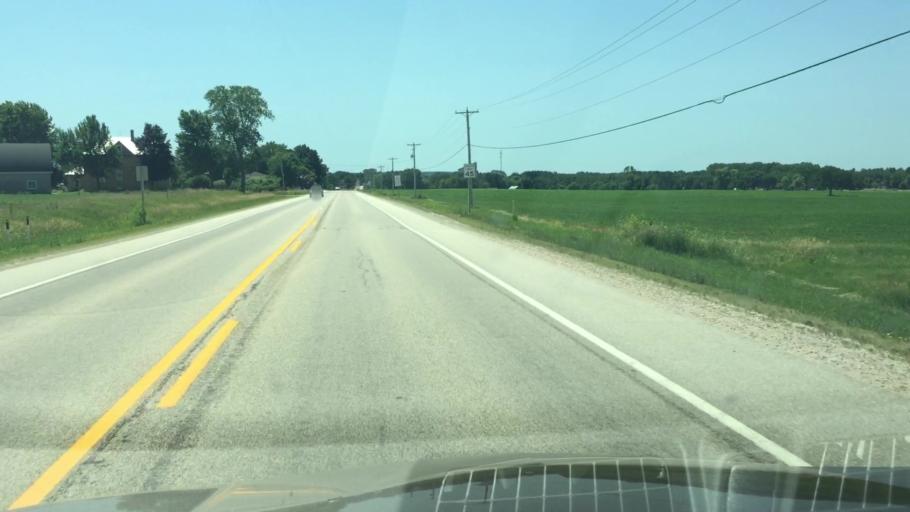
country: US
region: Wisconsin
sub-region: Fond du Lac County
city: Saint Peter
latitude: 43.9254
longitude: -88.3067
